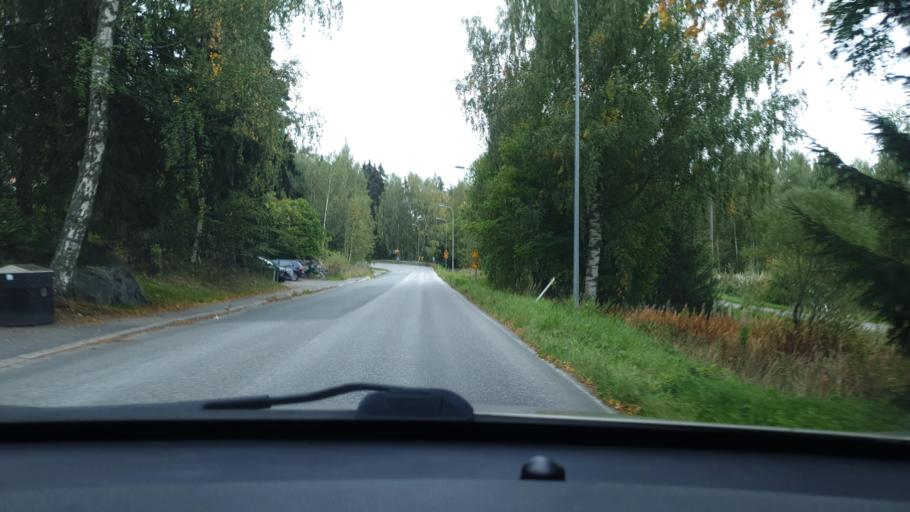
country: FI
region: Ostrobothnia
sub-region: Vaasa
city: Korsholm
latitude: 63.0977
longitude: 21.6615
